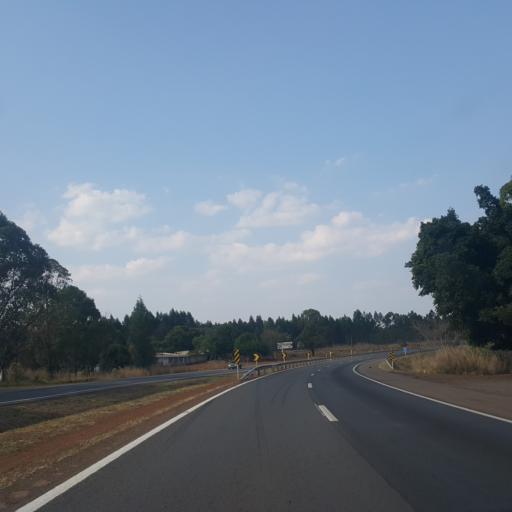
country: BR
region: Goias
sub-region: Abadiania
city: Abadiania
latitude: -16.1854
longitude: -48.6969
